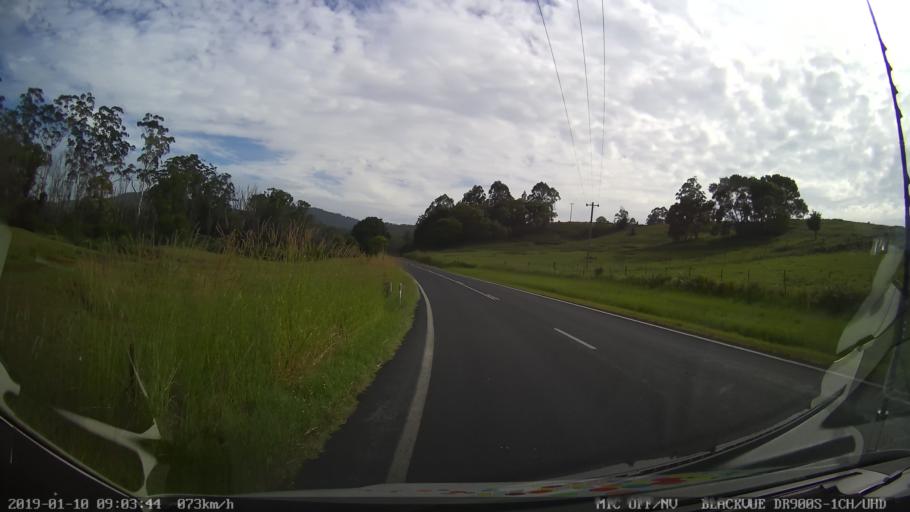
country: AU
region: New South Wales
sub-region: Coffs Harbour
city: Coffs Harbour
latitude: -30.2616
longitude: 153.0494
